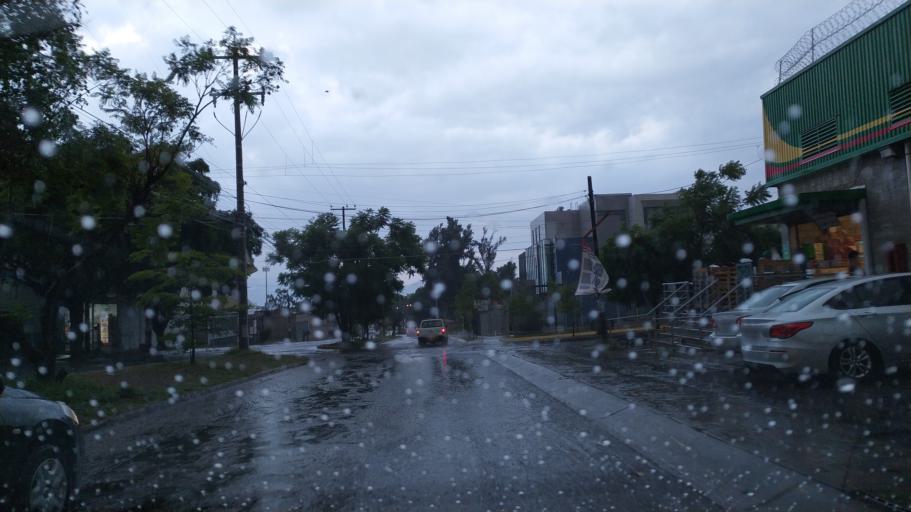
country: MX
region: Jalisco
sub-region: San Pedro Tlaquepaque
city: Paseo del Prado
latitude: 20.6086
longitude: -103.3958
